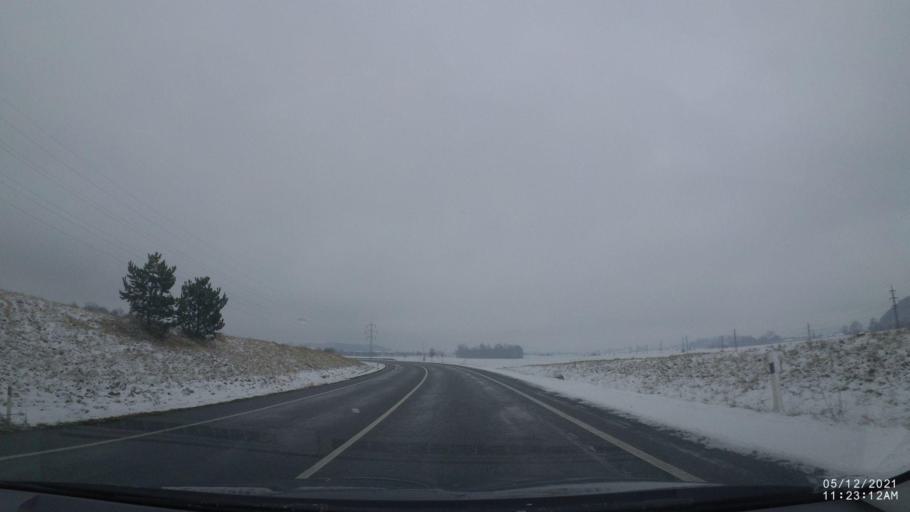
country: CZ
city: Solnice
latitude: 50.1948
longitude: 16.2395
